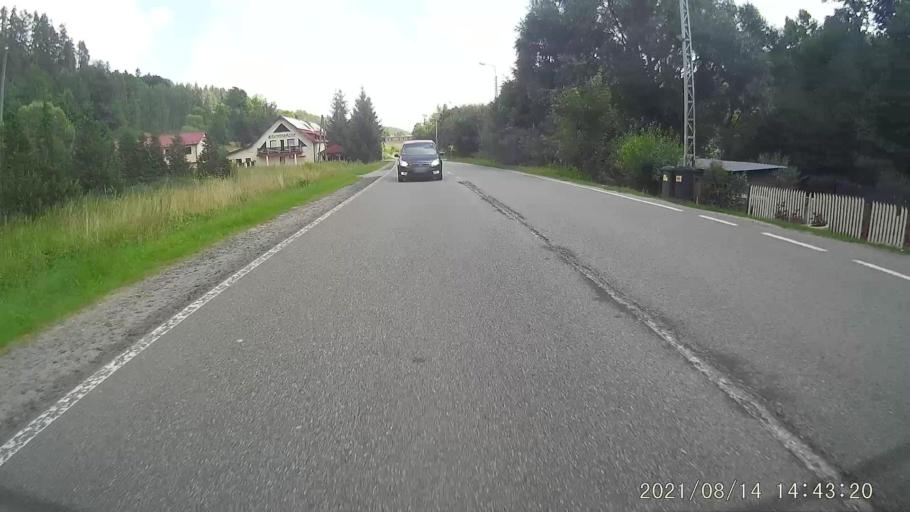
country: PL
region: Lower Silesian Voivodeship
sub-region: Powiat klodzki
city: Ludwikowice Klodzkie
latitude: 50.6256
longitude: 16.4565
